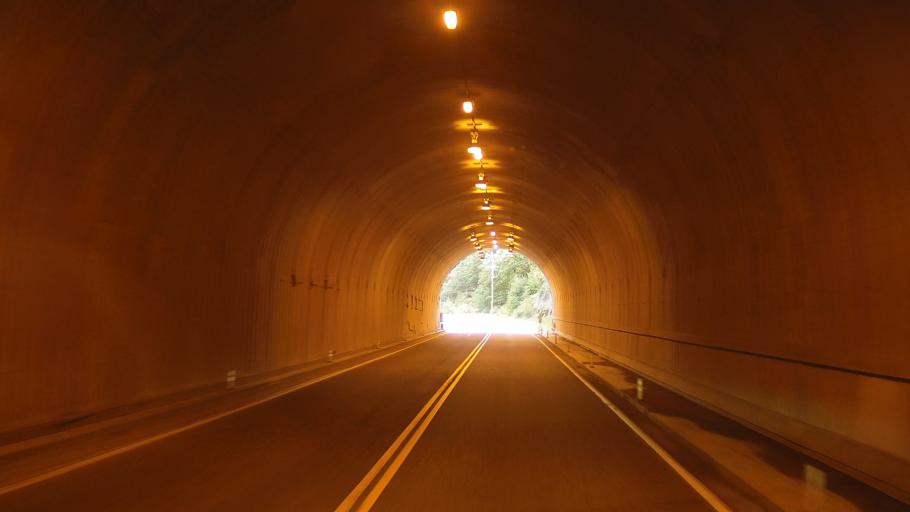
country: CA
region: British Columbia
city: Hope
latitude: 49.5912
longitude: -121.4090
